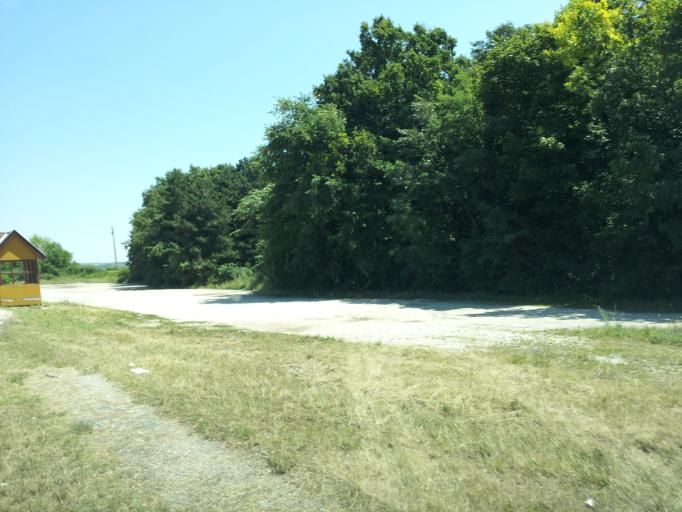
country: HU
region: Veszprem
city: Berhida
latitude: 47.1125
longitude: 18.1035
